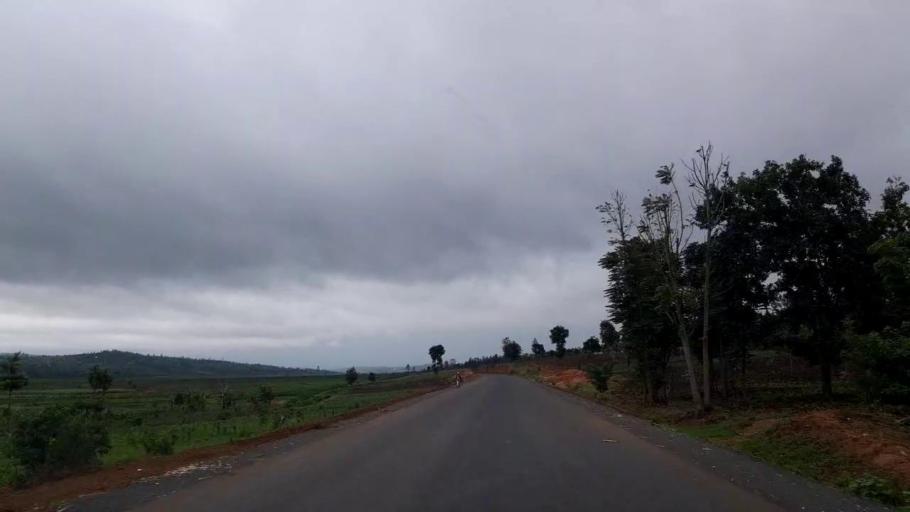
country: RW
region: Northern Province
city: Byumba
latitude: -1.4381
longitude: 30.2569
